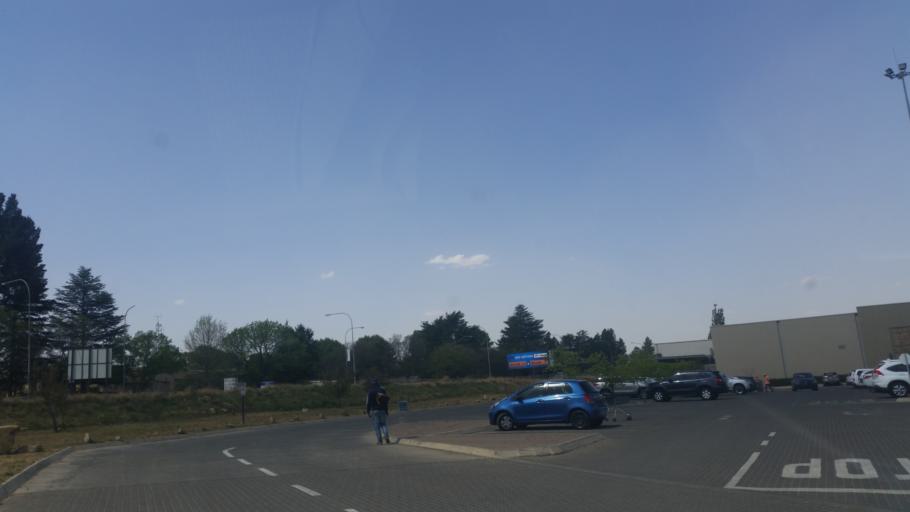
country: ZA
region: Orange Free State
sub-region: Thabo Mofutsanyana District Municipality
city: Bethlehem
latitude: -28.2403
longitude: 28.3247
